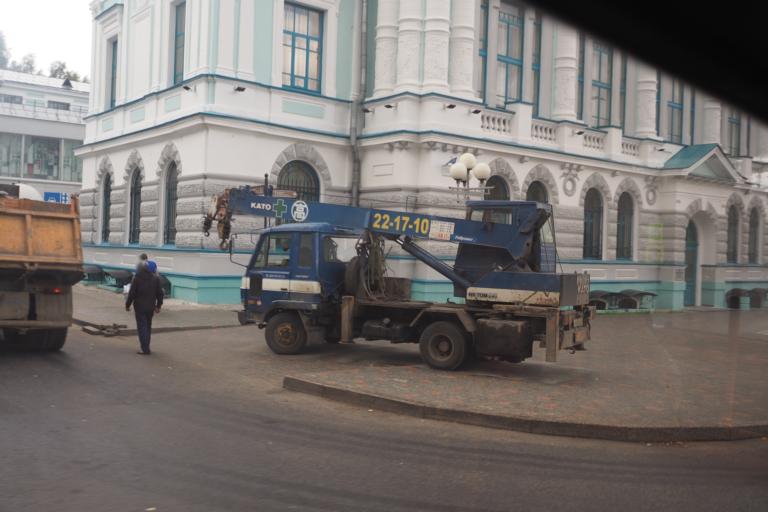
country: RU
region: Tomsk
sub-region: Tomskiy Rayon
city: Tomsk
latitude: 56.4676
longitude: 84.9504
